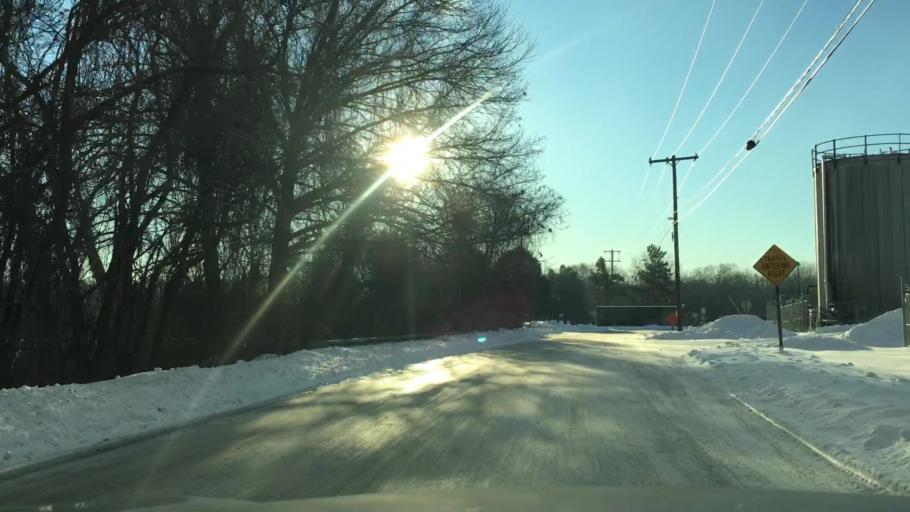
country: US
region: Massachusetts
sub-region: Hampden County
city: Springfield
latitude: 42.0912
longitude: -72.5900
